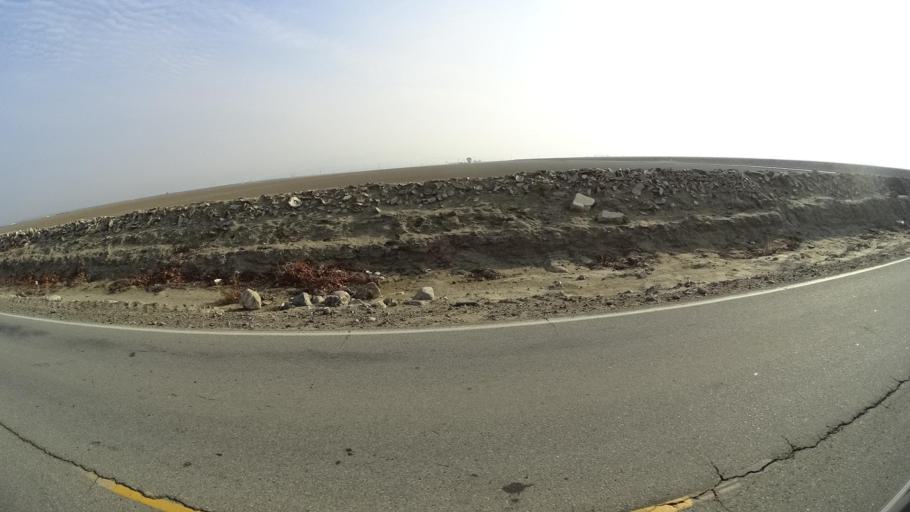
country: US
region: California
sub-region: Kern County
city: Weedpatch
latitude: 35.1012
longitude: -118.9147
